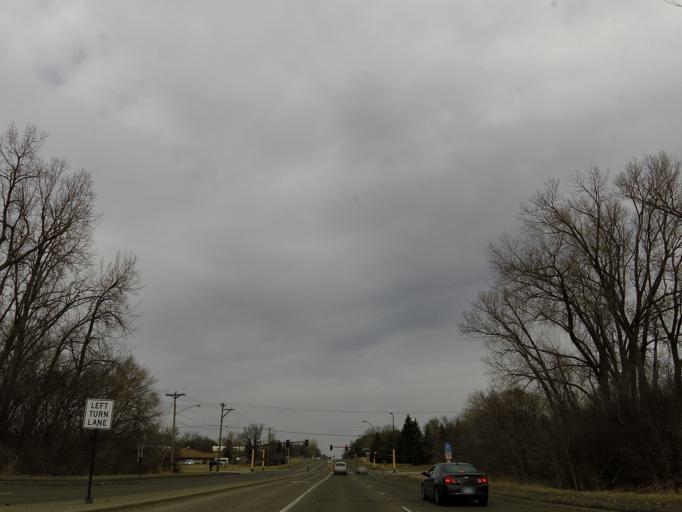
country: US
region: Minnesota
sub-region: Hennepin County
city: Bloomington
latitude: 44.8411
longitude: -93.3293
